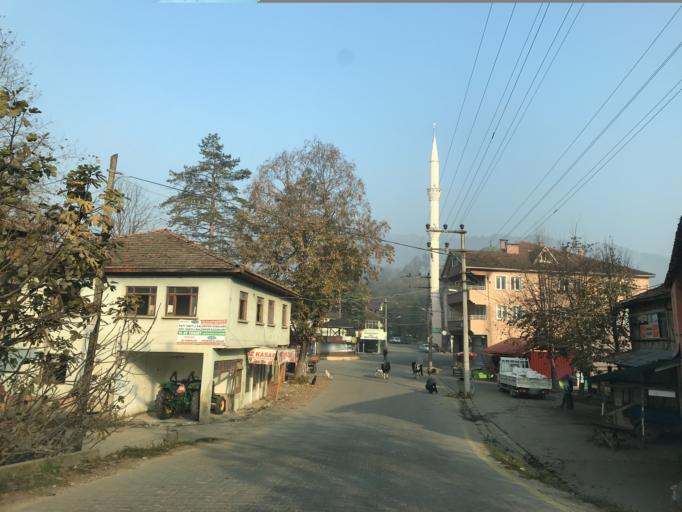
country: TR
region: Duzce
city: Cumayeri
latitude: 40.9076
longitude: 30.9507
